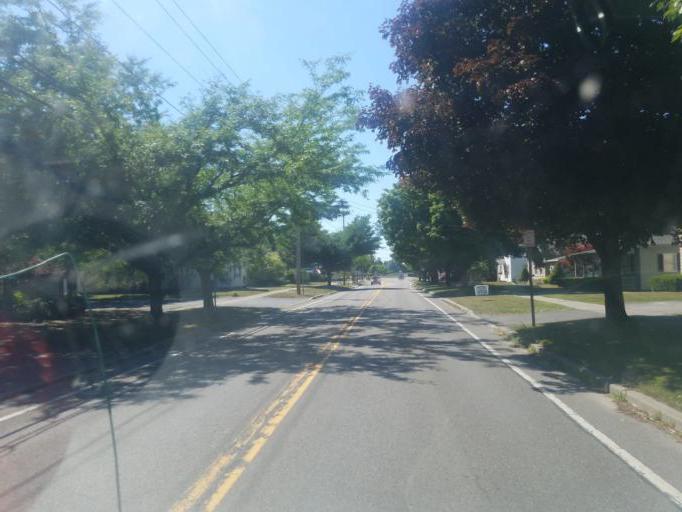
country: US
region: New York
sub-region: Ontario County
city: Phelps
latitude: 42.9619
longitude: -77.0731
